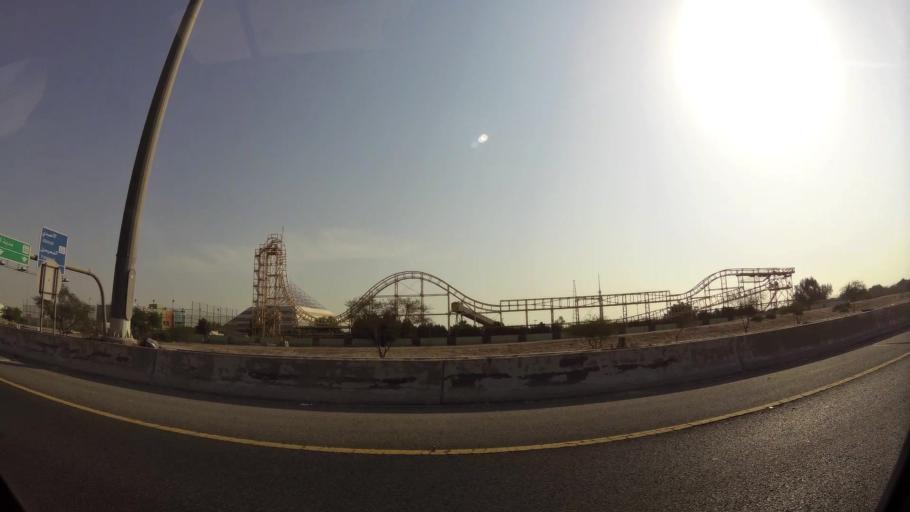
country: KW
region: Al Ahmadi
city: Al Ahmadi
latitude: 29.0886
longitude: 48.0987
